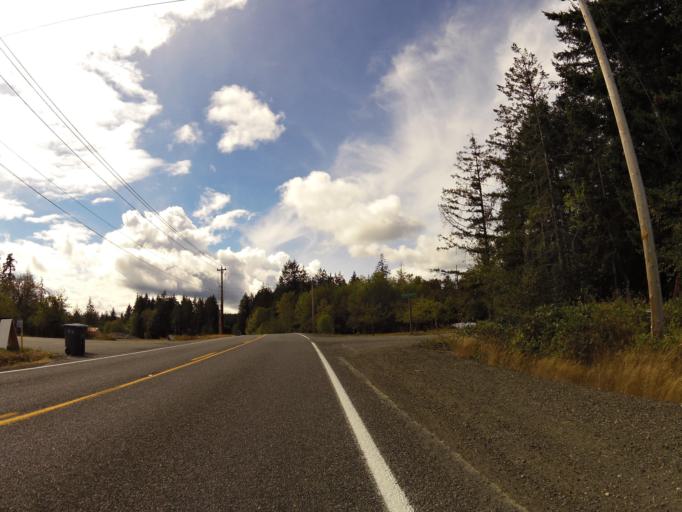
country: US
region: Washington
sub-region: Mason County
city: Shelton
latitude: 47.1527
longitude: -123.0595
